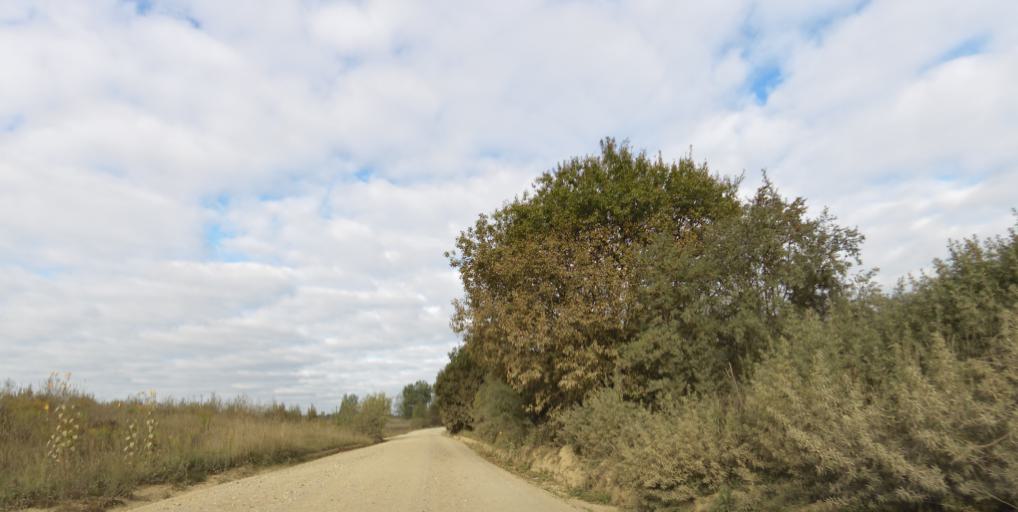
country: LT
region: Vilnius County
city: Pilaite
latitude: 54.7307
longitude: 25.1641
